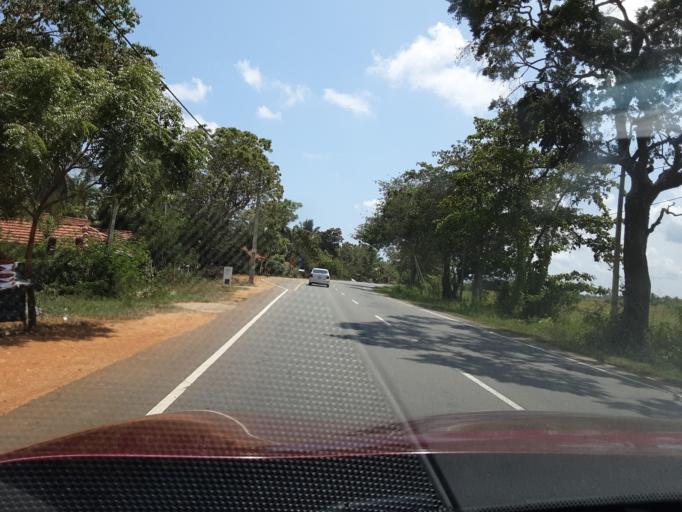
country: LK
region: Southern
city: Tangalla
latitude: 6.2217
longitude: 81.2178
